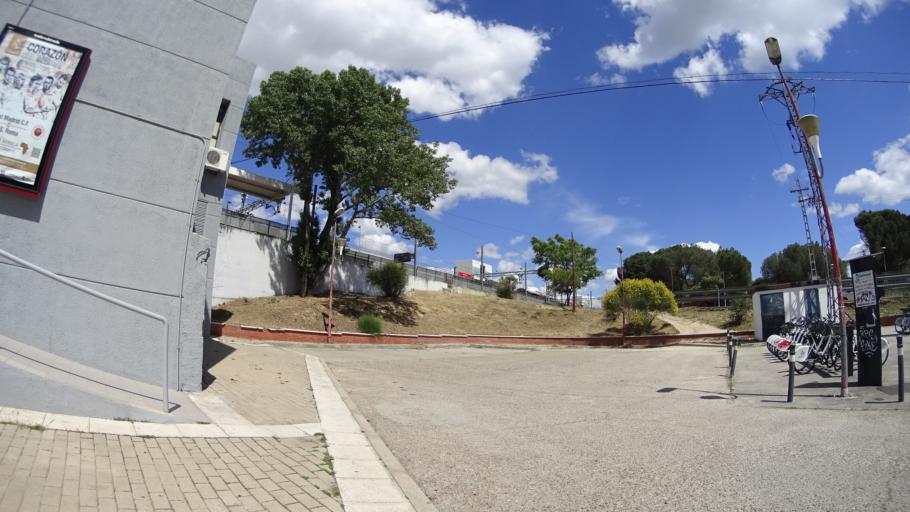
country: ES
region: Madrid
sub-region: Provincia de Madrid
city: Majadahonda
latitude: 40.4741
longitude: -3.8463
